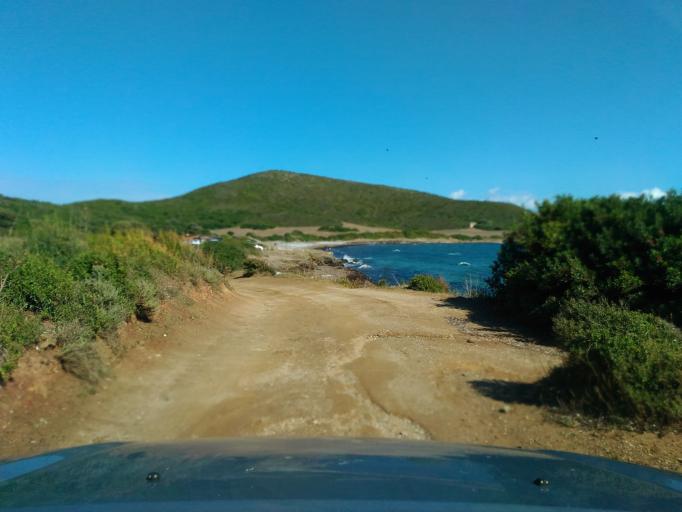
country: FR
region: Corsica
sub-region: Departement de la Haute-Corse
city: Brando
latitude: 42.9731
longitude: 9.4537
